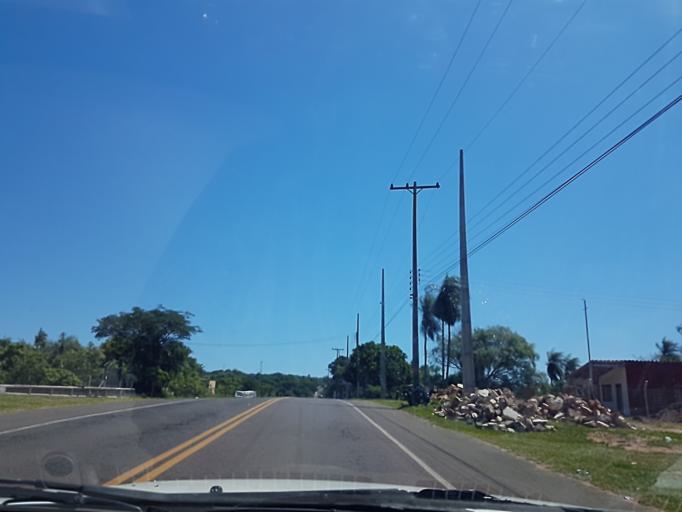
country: PY
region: Cordillera
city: Altos
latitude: -25.2546
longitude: -57.2428
